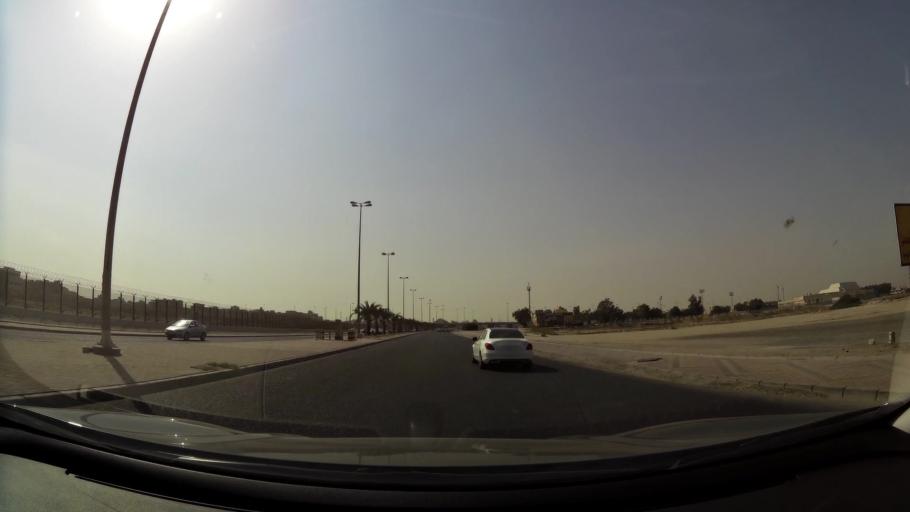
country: KW
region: Al Ahmadi
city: Al Manqaf
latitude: 29.1196
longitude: 48.1238
